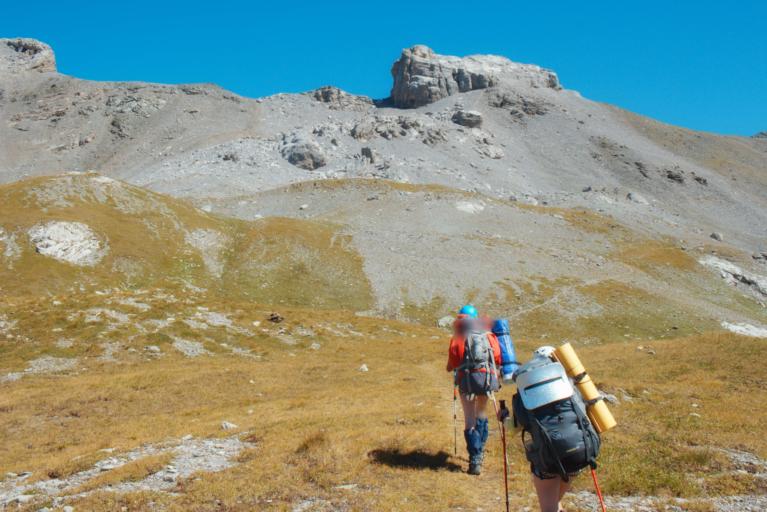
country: RU
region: Karachayevo-Cherkesiya
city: Nizhniy Arkhyz
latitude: 43.5948
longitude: 41.1793
